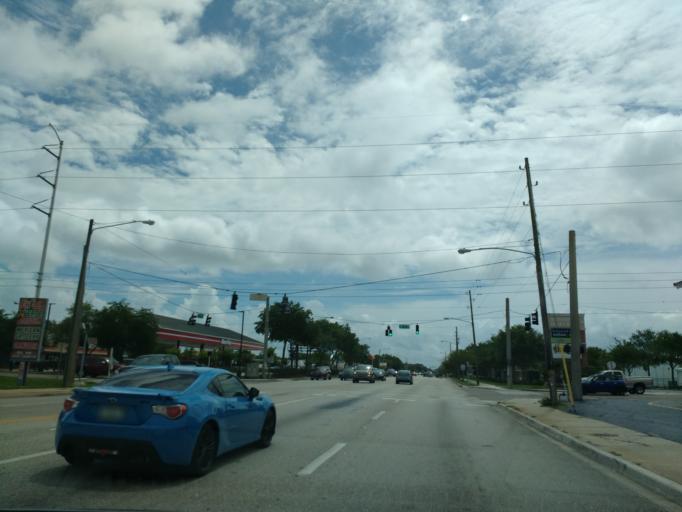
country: US
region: Florida
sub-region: Pinellas County
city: Saint Petersburg
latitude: 27.7919
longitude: -82.6718
